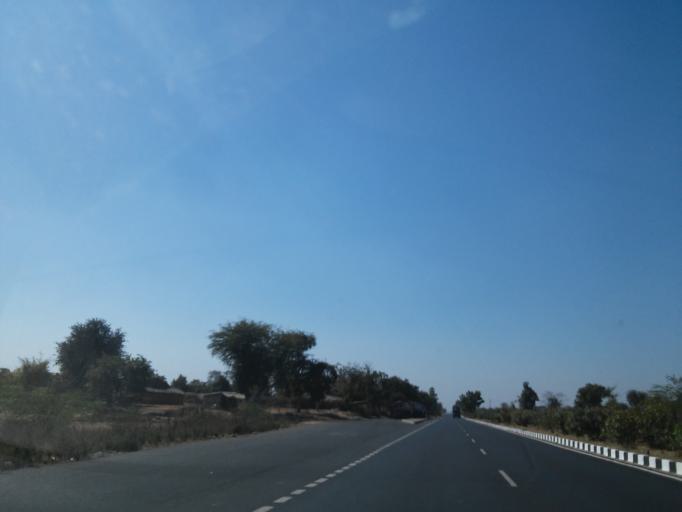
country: IN
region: Gujarat
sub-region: Sabar Kantha
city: Modasa
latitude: 23.6711
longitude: 73.3385
